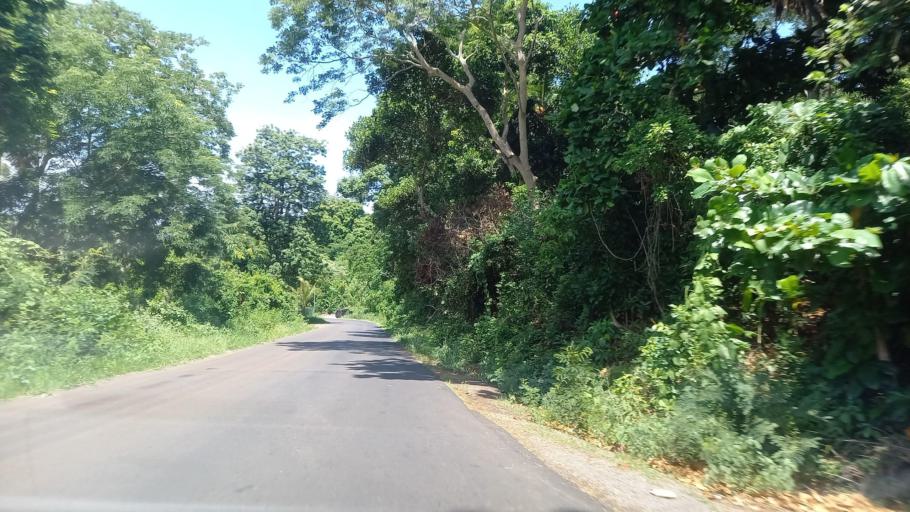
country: YT
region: M'Tsangamouji
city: M'Tsangamouji
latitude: -12.7487
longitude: 45.0632
